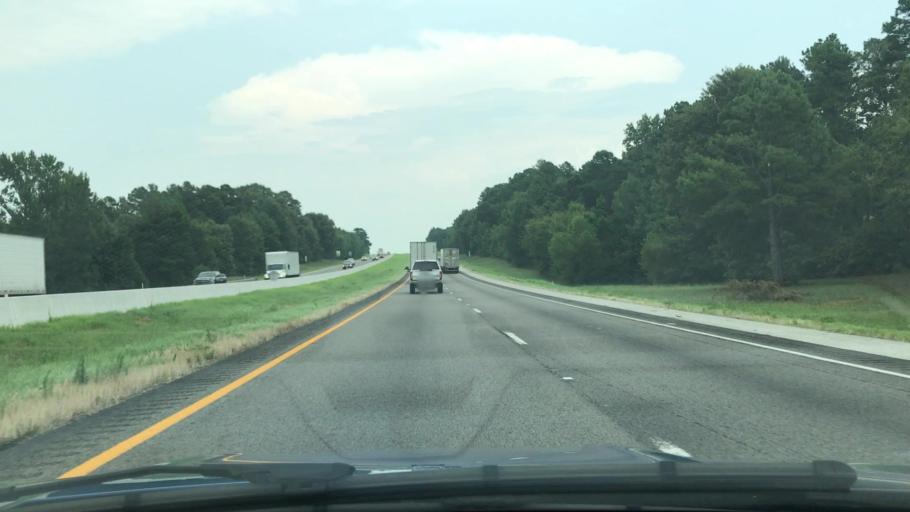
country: US
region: Texas
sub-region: Gregg County
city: Liberty City
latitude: 32.4367
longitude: -95.0049
